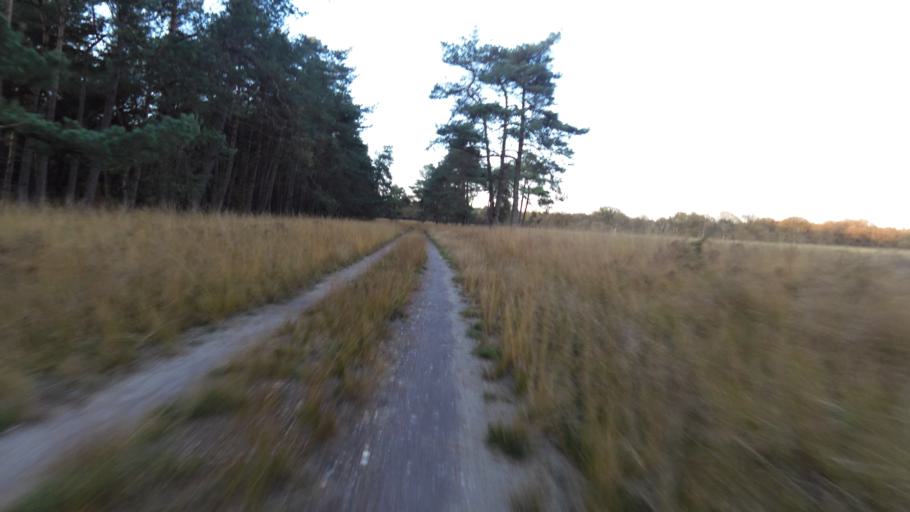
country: NL
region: Gelderland
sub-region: Gemeente Apeldoorn
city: Uddel
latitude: 52.2922
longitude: 5.8386
